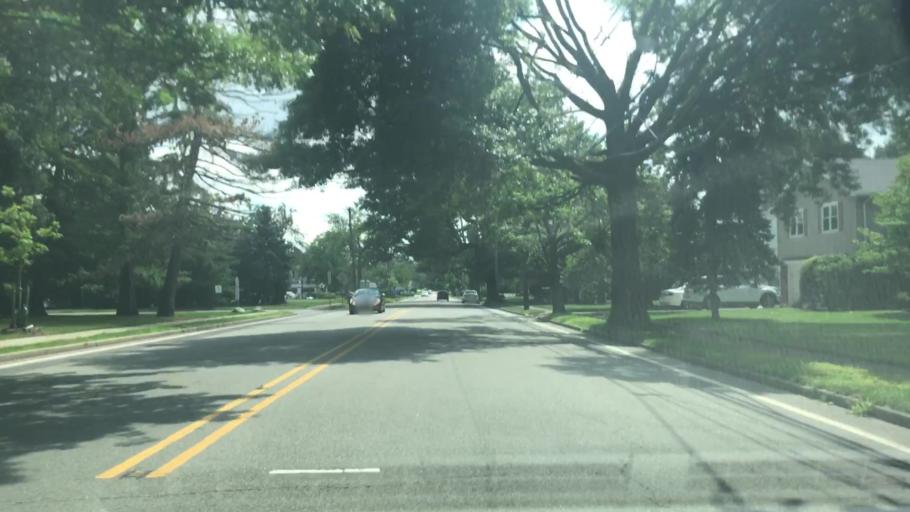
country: US
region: New Jersey
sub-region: Passaic County
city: Clifton
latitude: 40.8527
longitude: -74.1795
